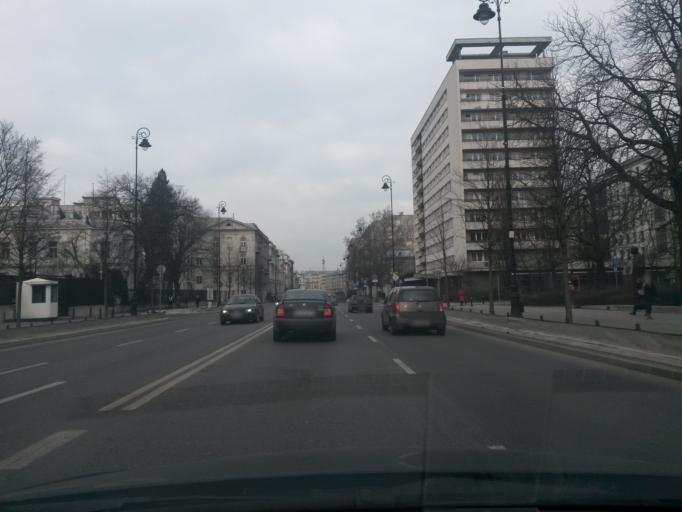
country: PL
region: Masovian Voivodeship
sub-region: Warszawa
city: Srodmiescie
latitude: 52.2244
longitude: 21.0240
